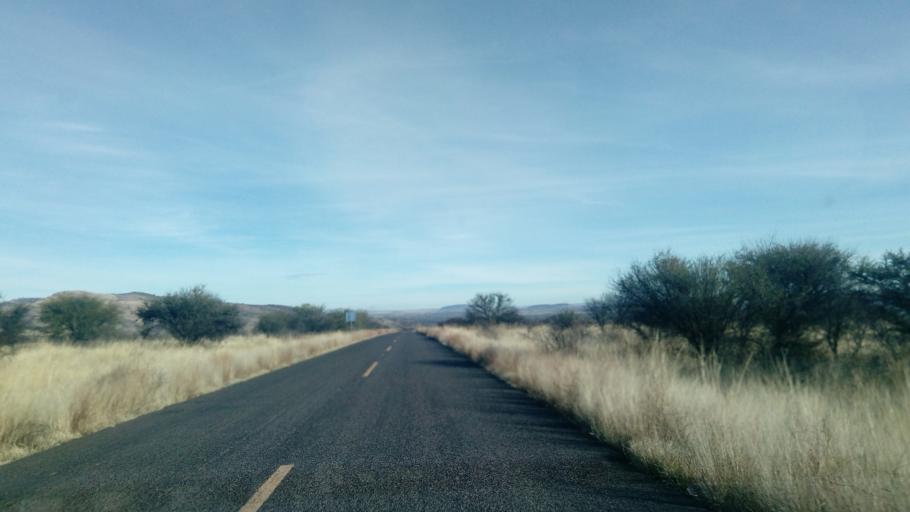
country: MX
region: Durango
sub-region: Nombre de Dios
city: Nombre de Dios
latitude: 23.9299
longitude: -104.3330
